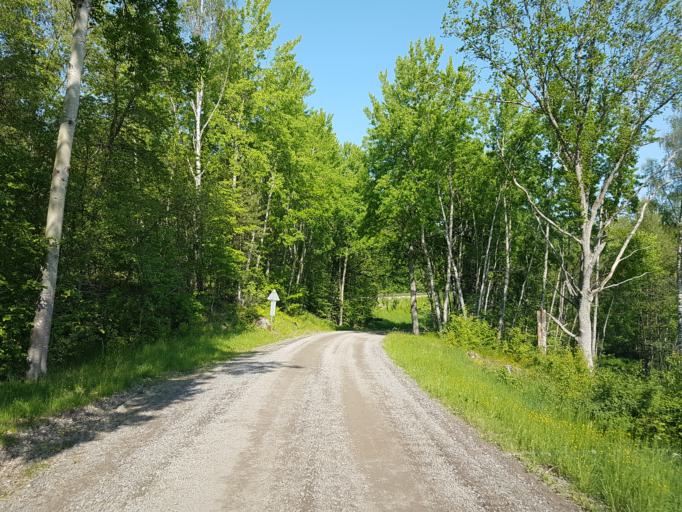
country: SE
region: OEstergoetland
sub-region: Atvidabergs Kommun
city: Atvidaberg
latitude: 58.1815
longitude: 16.1126
